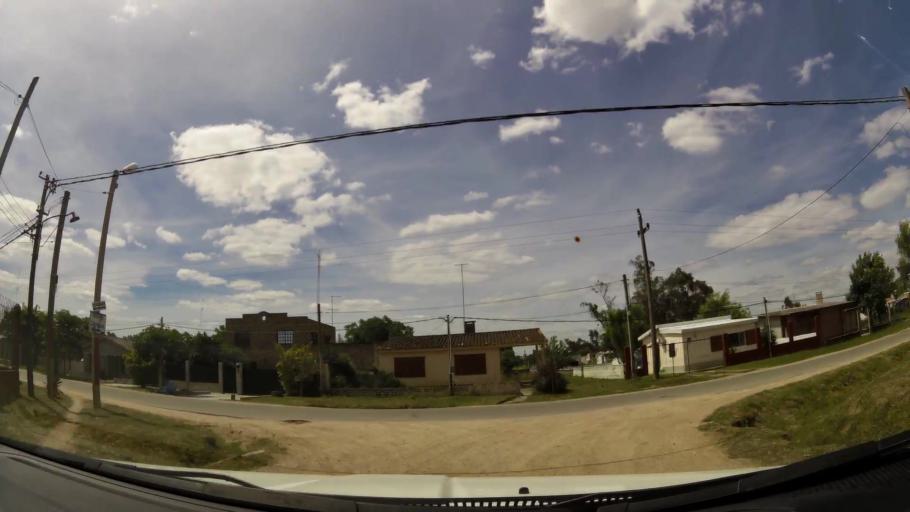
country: UY
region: San Jose
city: Delta del Tigre
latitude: -34.7491
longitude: -56.4567
